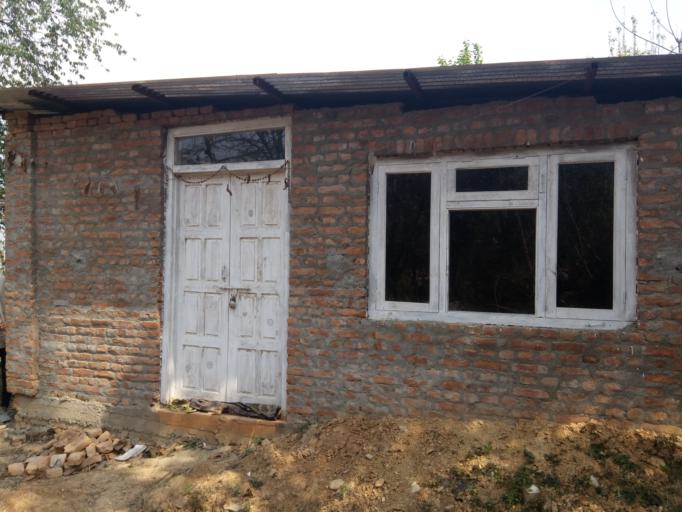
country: NP
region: Central Region
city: Kirtipur
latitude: 27.5949
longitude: 85.2622
